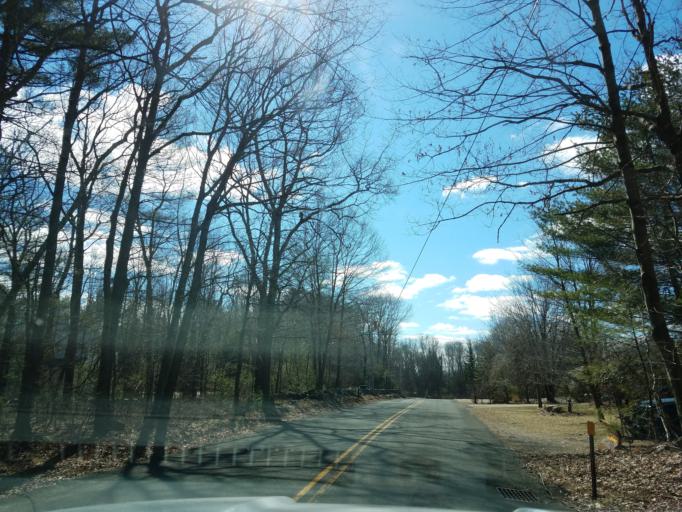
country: US
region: Connecticut
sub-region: Windham County
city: North Grosvenor Dale
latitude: 41.9967
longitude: -71.8827
